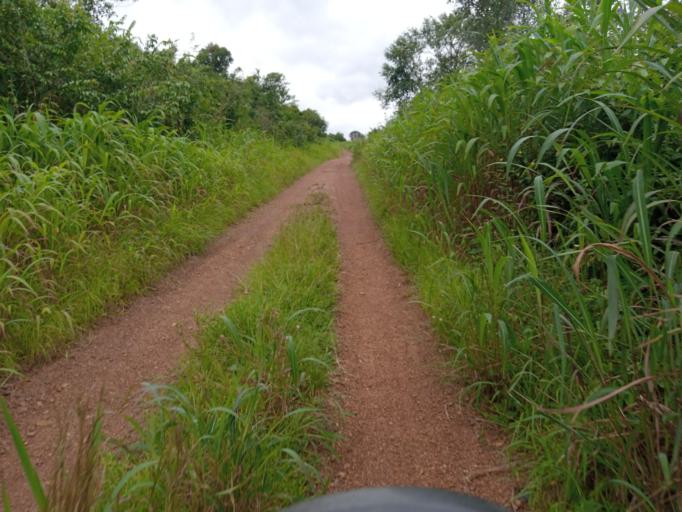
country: SL
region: Southern Province
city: Largo
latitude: 8.1987
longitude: -12.0512
